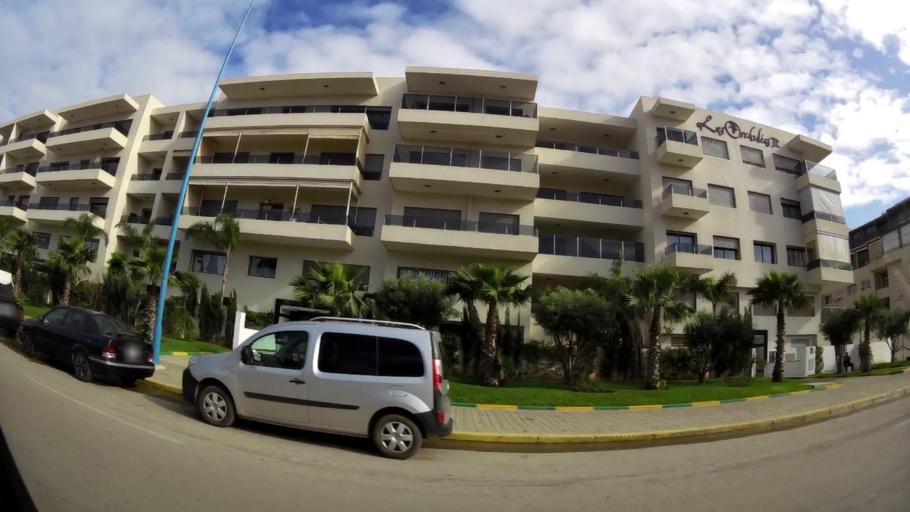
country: MA
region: Grand Casablanca
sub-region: Mohammedia
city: Mohammedia
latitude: 33.7127
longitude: -7.3422
